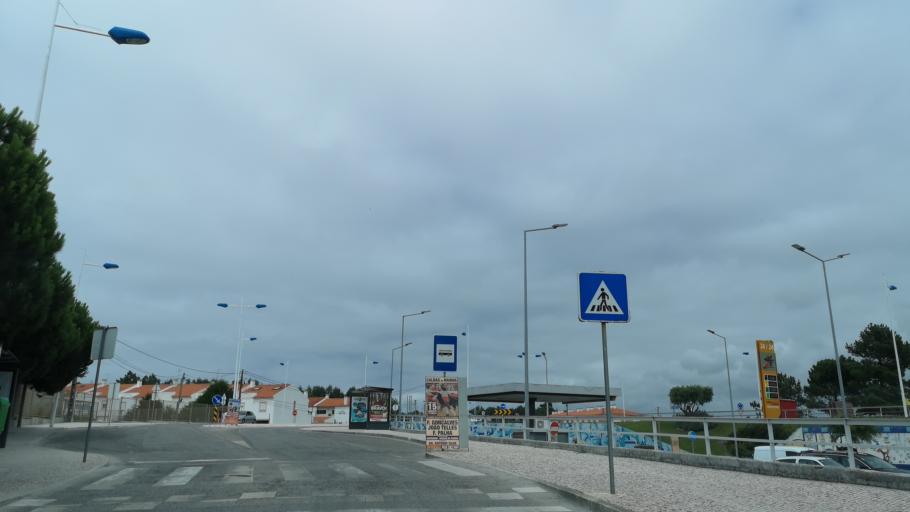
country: PT
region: Leiria
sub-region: Nazare
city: Nazare
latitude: 39.5151
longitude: -9.1263
